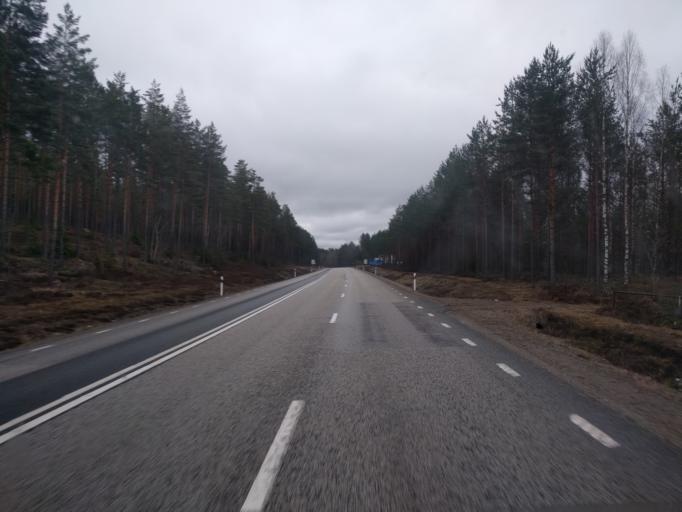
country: SE
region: Joenkoeping
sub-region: Eksjo Kommun
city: Haljarp
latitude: 57.6403
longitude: 15.2947
